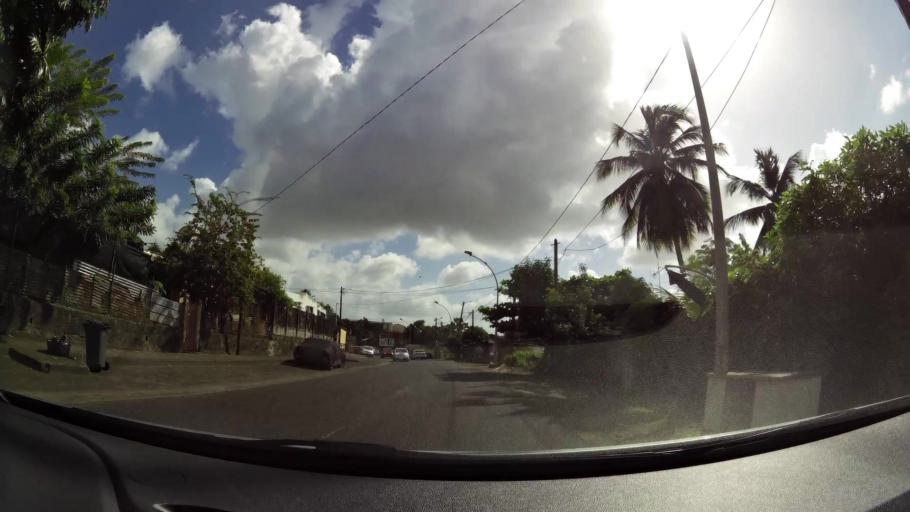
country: MQ
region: Martinique
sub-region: Martinique
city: Le Lamentin
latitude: 14.6130
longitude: -61.0050
